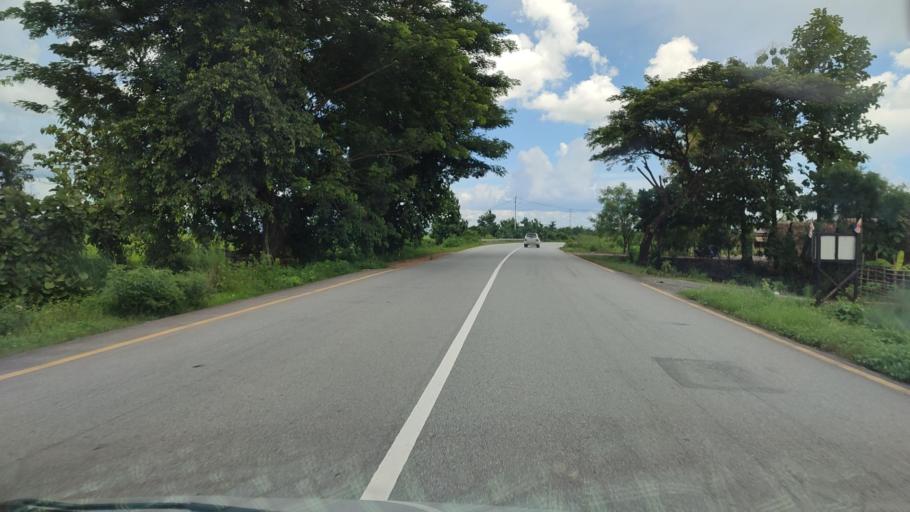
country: MM
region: Bago
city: Nyaunglebin
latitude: 18.0092
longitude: 96.6990
